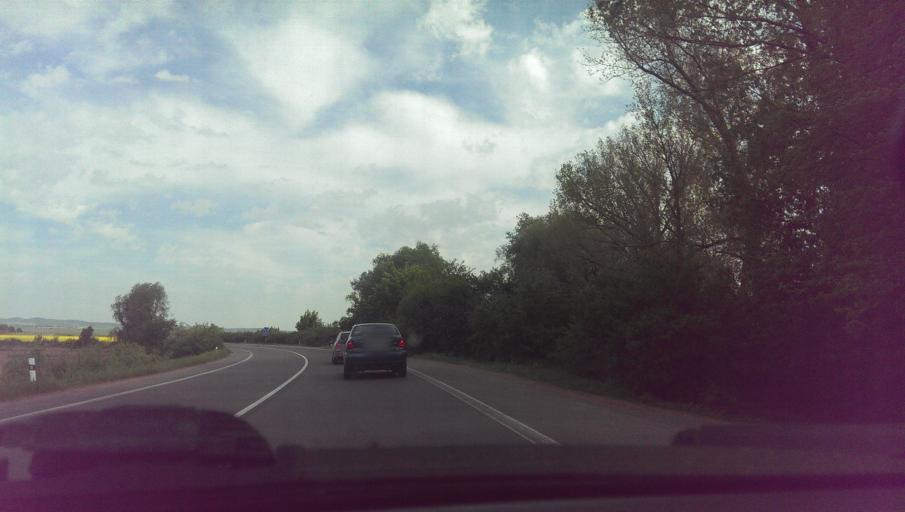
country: CZ
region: Zlin
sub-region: Okres Uherske Hradiste
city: Stare Mesto
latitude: 49.0875
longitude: 17.4492
